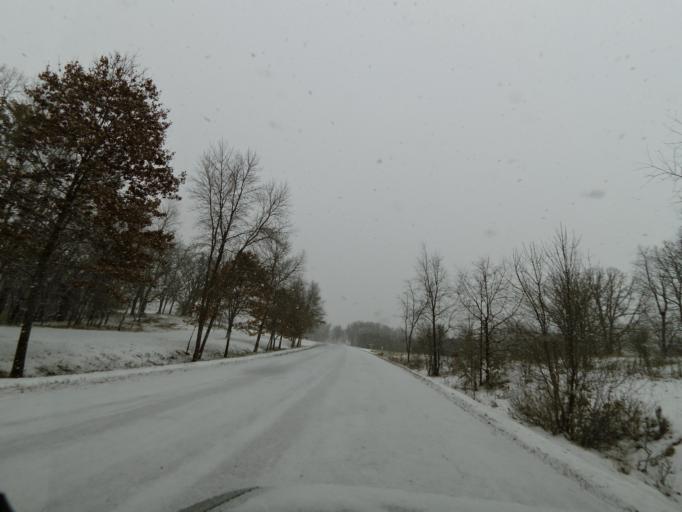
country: US
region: Minnesota
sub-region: Washington County
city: Lake Elmo
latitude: 44.9803
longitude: -92.9008
